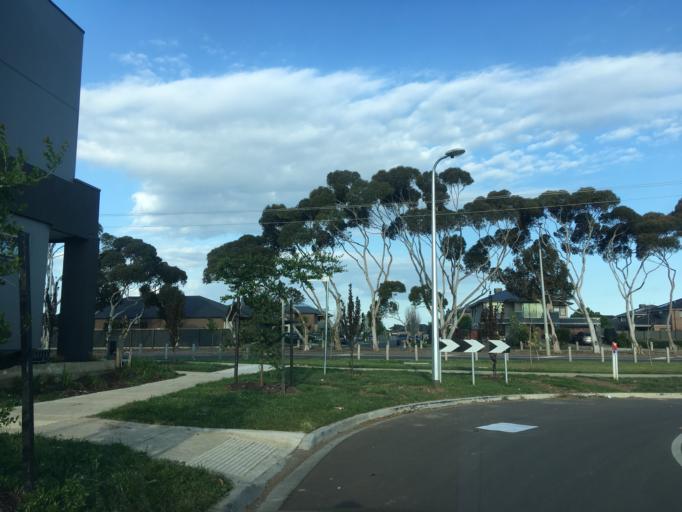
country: AU
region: Victoria
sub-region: Wyndham
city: Hoppers Crossing
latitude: -37.8849
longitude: 144.7183
